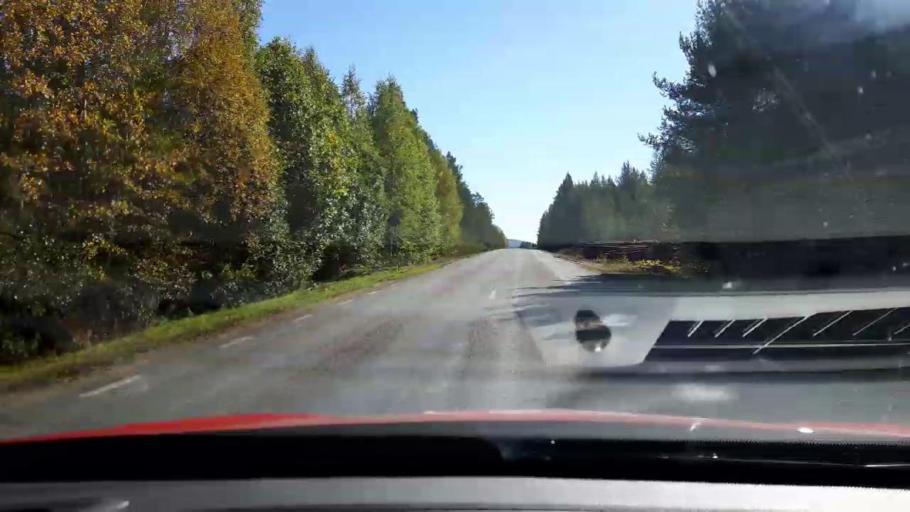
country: SE
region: Jaemtland
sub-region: Harjedalens Kommun
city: Sveg
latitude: 62.3075
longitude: 14.0465
